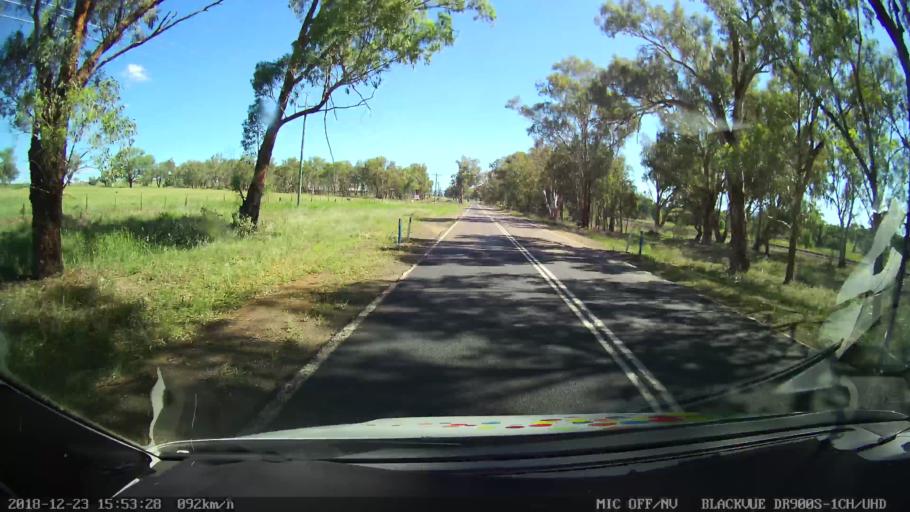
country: AU
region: New South Wales
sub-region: Tamworth Municipality
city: Phillip
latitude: -31.1334
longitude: 150.8807
